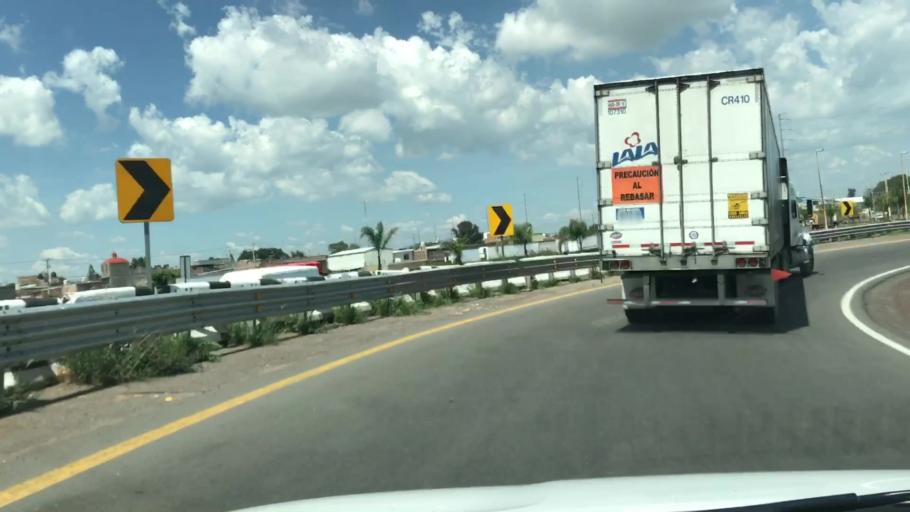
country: MX
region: Guanajuato
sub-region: Irapuato
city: Las Huertas Tercera Seccion
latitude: 20.6508
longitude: -101.3750
